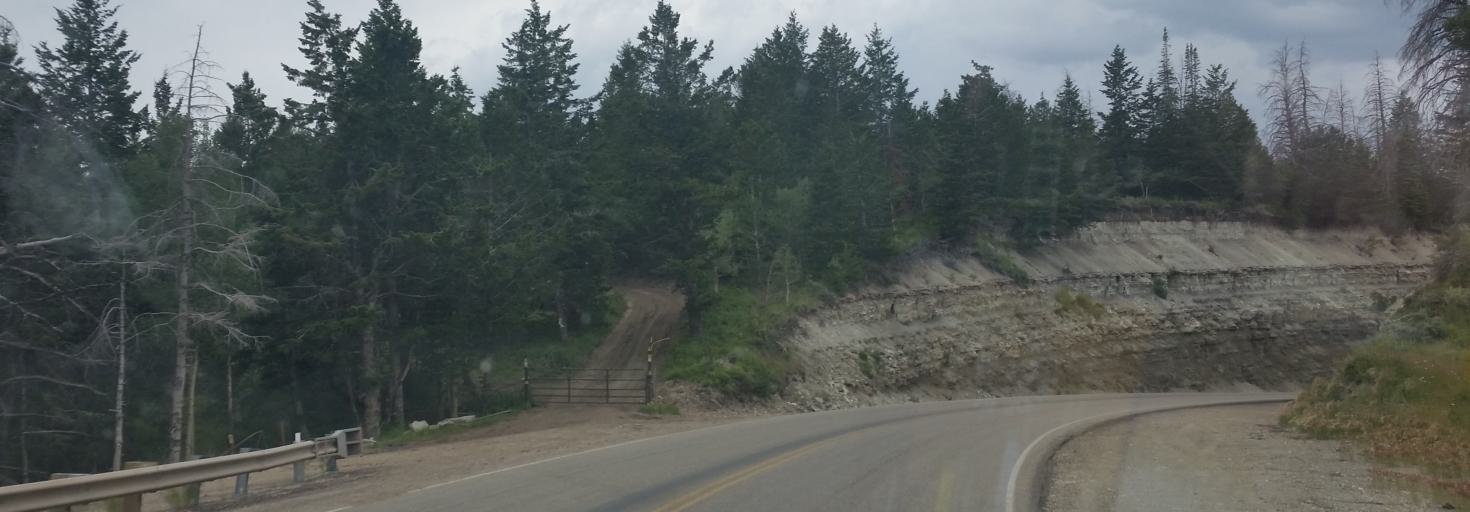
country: US
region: Utah
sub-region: Carbon County
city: Helper
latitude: 39.8782
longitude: -110.7524
